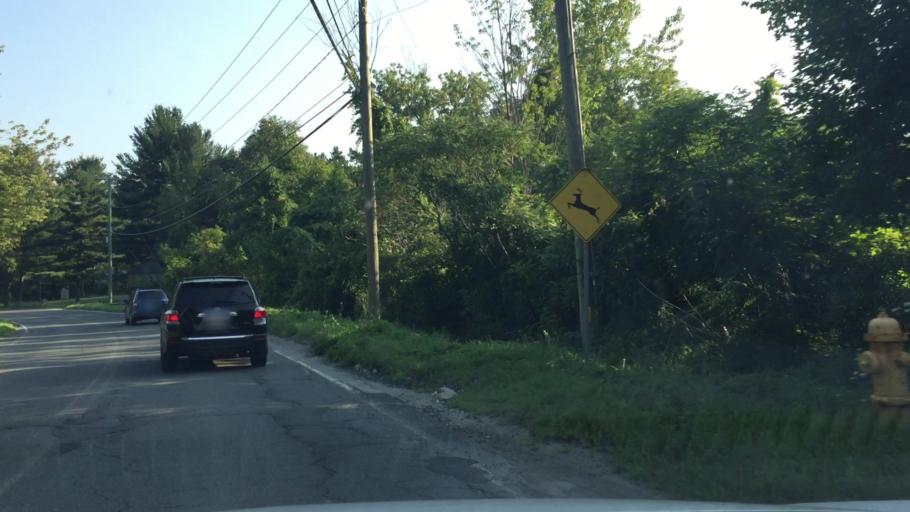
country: US
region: Massachusetts
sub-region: Berkshire County
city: Dalton
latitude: 42.4614
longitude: -73.1887
